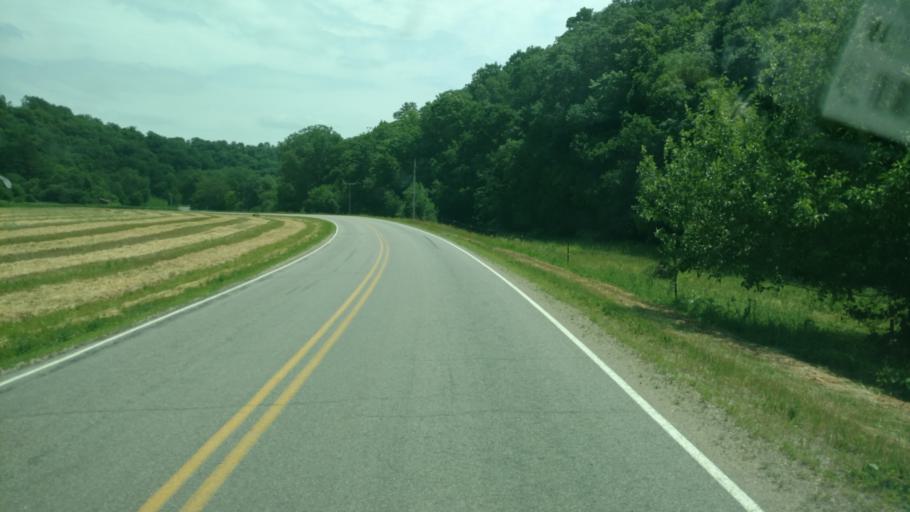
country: US
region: Wisconsin
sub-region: Monroe County
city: Cashton
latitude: 43.6606
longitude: -90.7204
